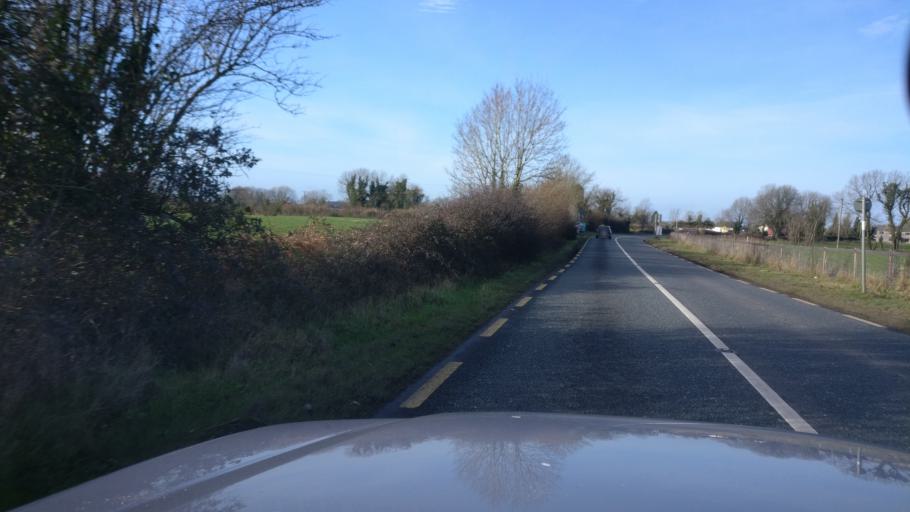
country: IE
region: Leinster
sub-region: Laois
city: Mountmellick
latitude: 53.1476
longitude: -7.3688
